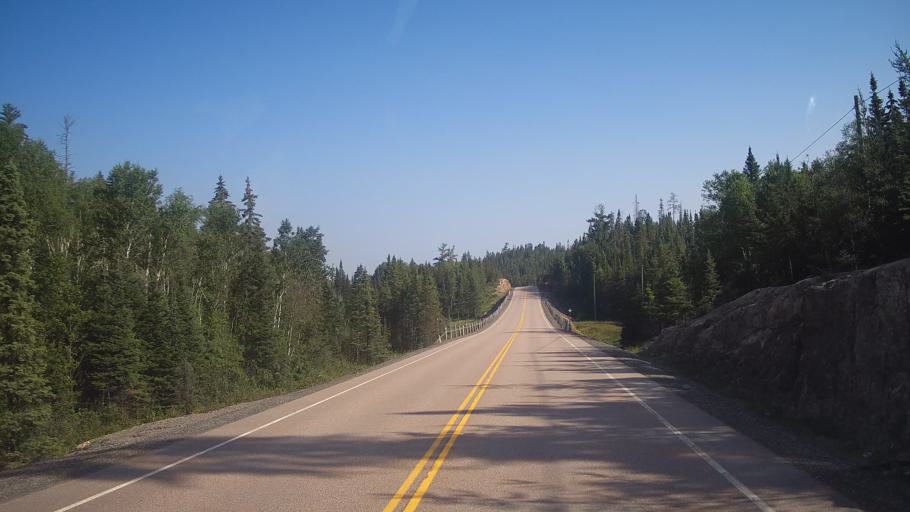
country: CA
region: Ontario
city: Rayside-Balfour
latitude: 47.0085
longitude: -81.6333
